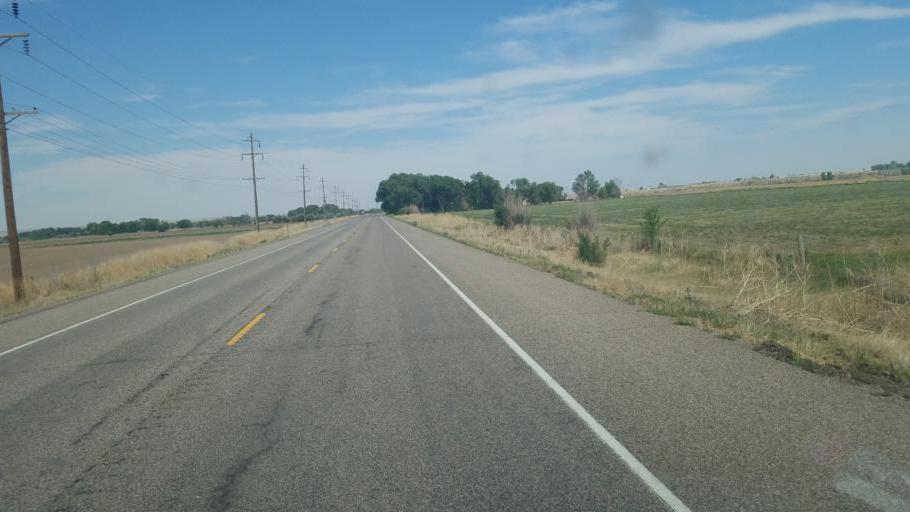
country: US
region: Colorado
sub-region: Otero County
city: Fowler
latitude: 38.2287
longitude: -104.2748
